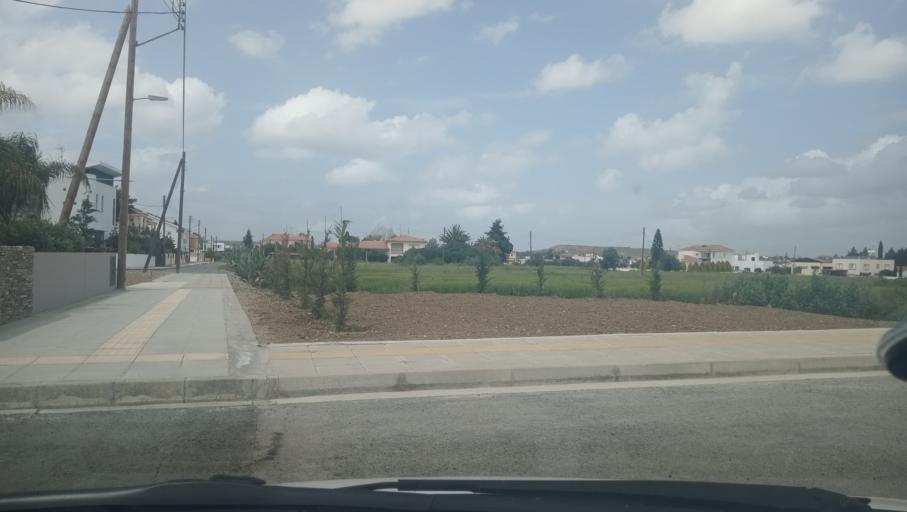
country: CY
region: Lefkosia
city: Pano Deftera
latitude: 35.0762
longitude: 33.2691
